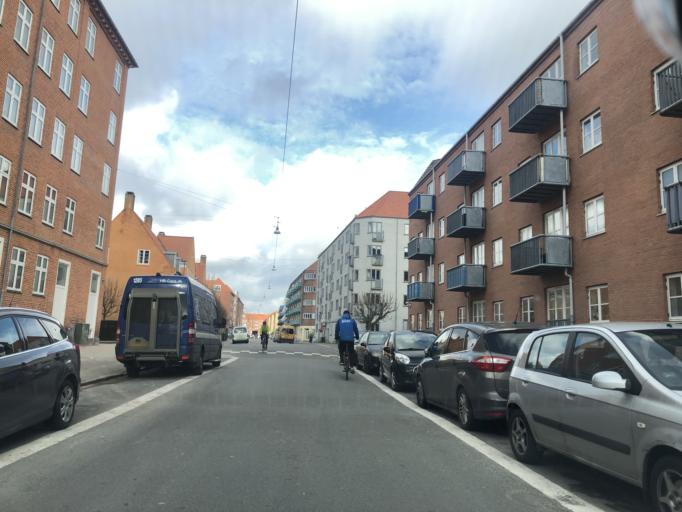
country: DK
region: Capital Region
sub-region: Tarnby Kommune
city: Tarnby
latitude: 55.6513
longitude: 12.6165
